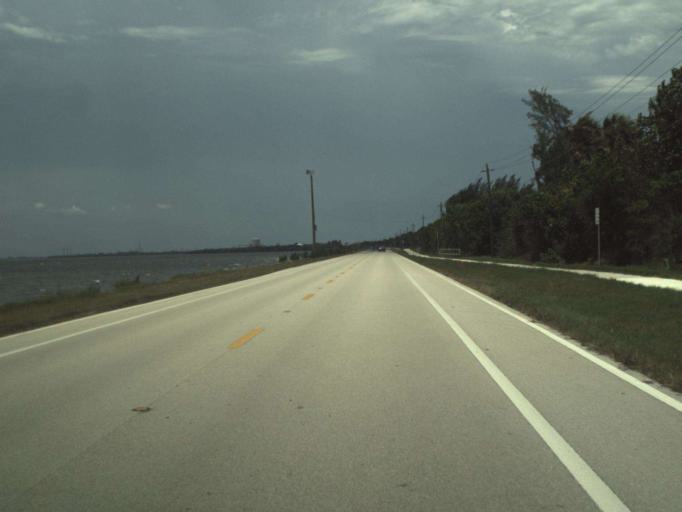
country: US
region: Florida
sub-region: Saint Lucie County
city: Hutchinson Island South
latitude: 27.3090
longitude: -80.2220
